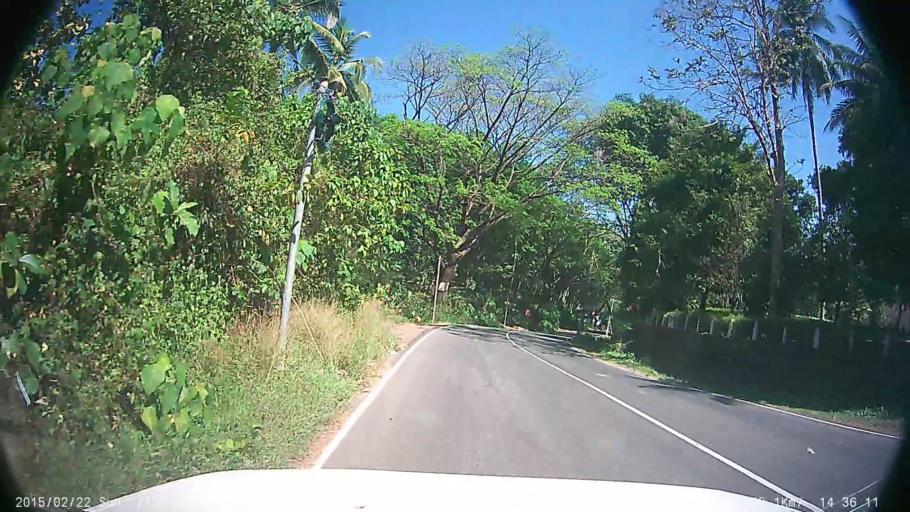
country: IN
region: Kerala
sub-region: Kottayam
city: Erattupetta
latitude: 9.5545
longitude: 76.7863
